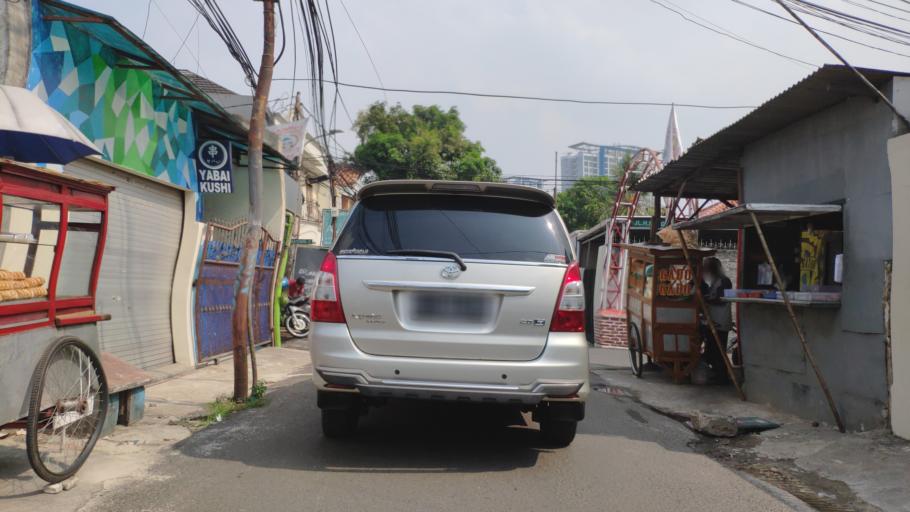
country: ID
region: Banten
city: South Tangerang
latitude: -6.2864
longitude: 106.7900
